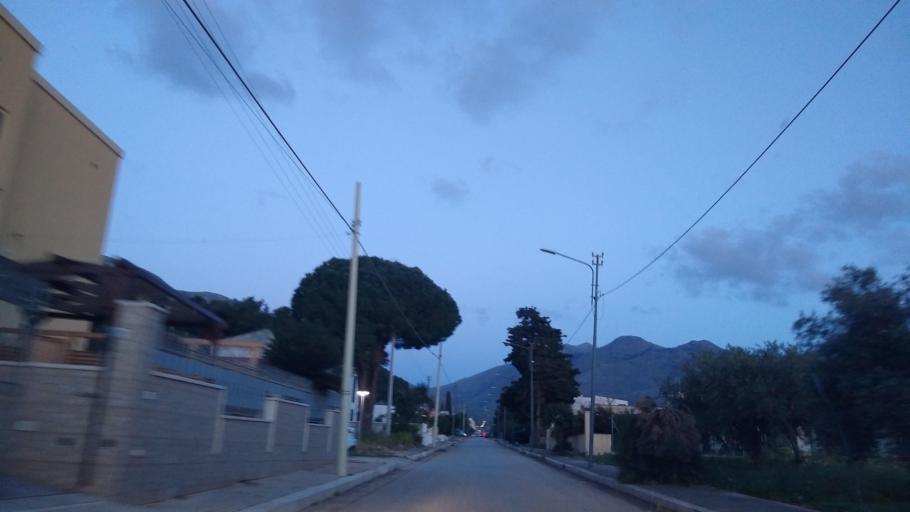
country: IT
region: Sicily
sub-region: Trapani
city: Castelluzzo
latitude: 38.1045
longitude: 12.7317
